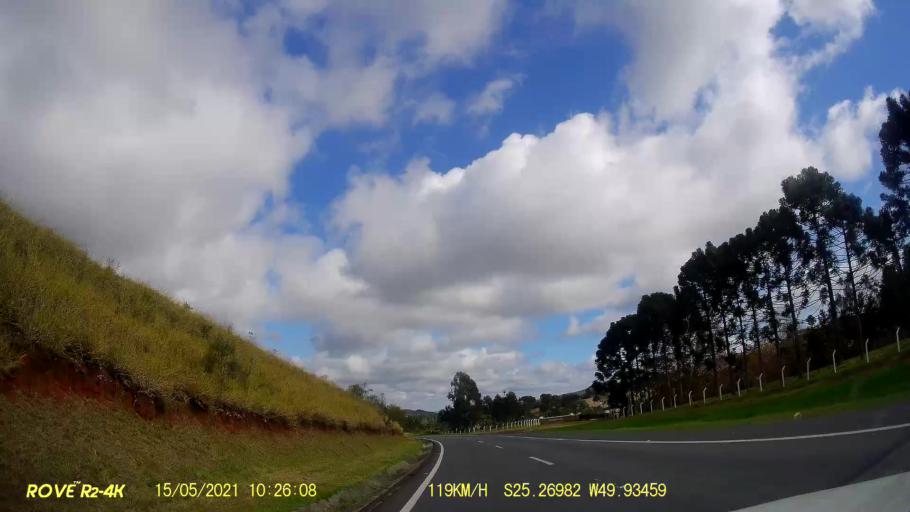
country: BR
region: Parana
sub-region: Palmeira
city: Palmeira
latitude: -25.2704
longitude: -49.9348
